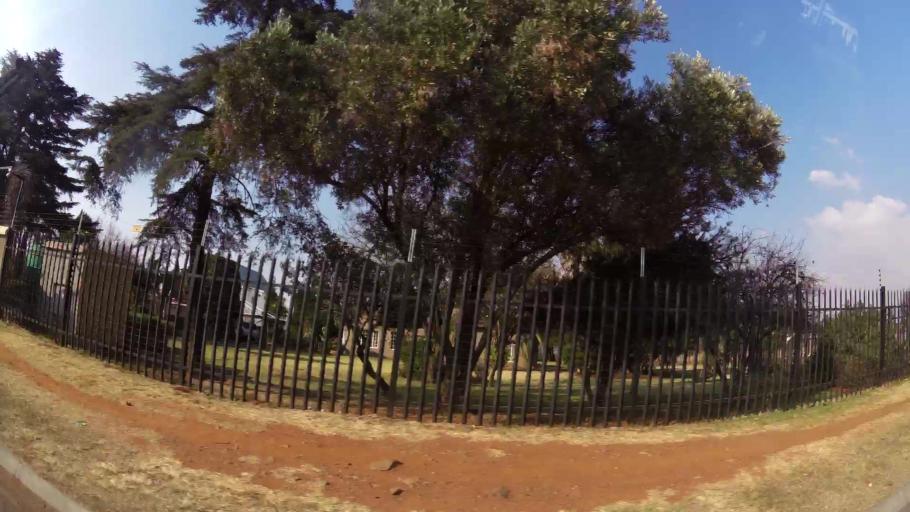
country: ZA
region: Gauteng
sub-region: Ekurhuleni Metropolitan Municipality
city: Boksburg
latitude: -26.1959
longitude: 28.2539
